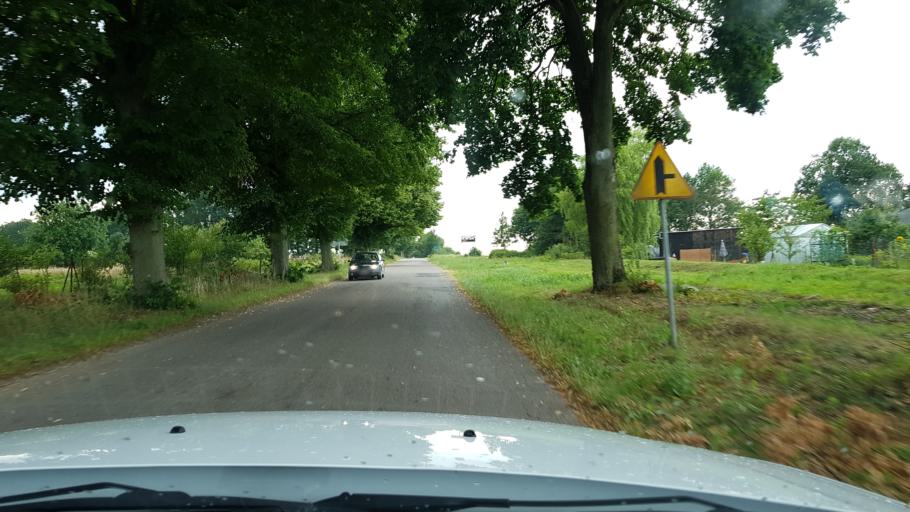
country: PL
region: West Pomeranian Voivodeship
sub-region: Powiat walecki
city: Walcz
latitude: 53.3490
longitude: 16.3925
